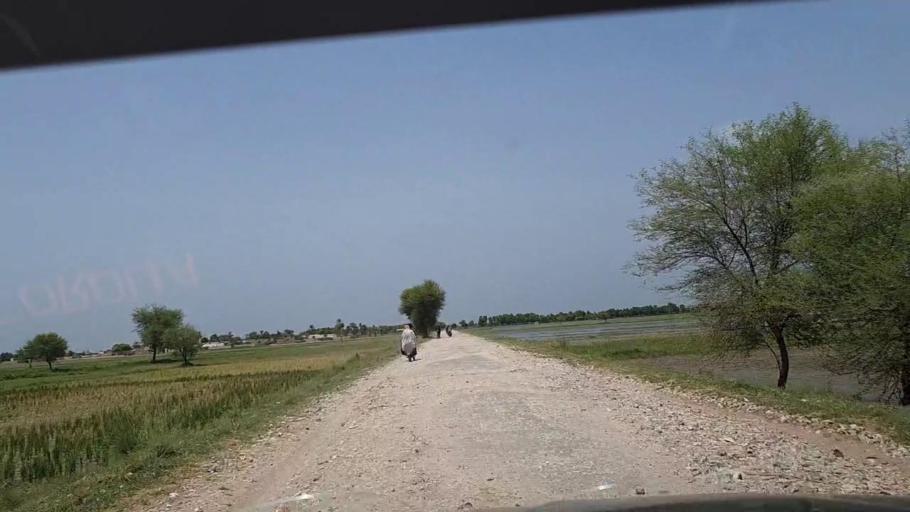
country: PK
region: Sindh
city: Khanpur
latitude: 27.8201
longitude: 69.4444
